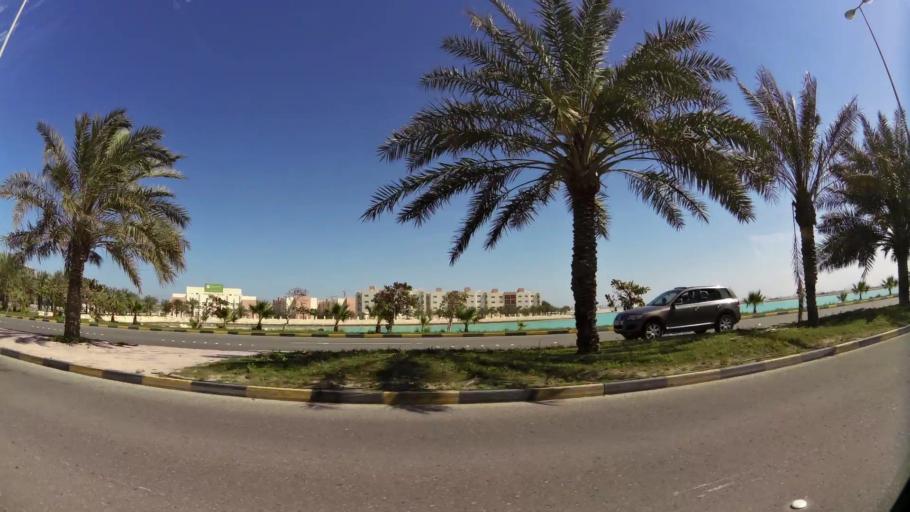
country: BH
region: Muharraq
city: Al Hadd
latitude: 26.2779
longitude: 50.6629
